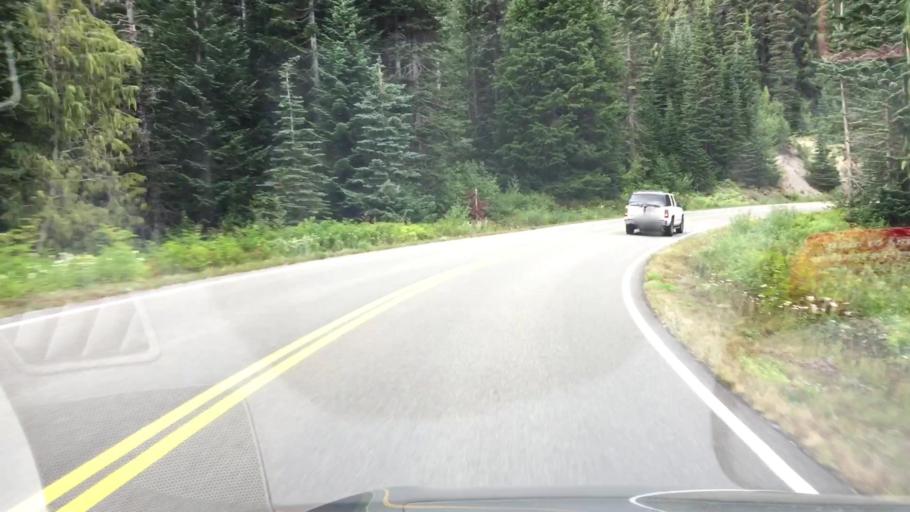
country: US
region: Washington
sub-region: Pierce County
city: Buckley
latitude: 46.7714
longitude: -121.7064
